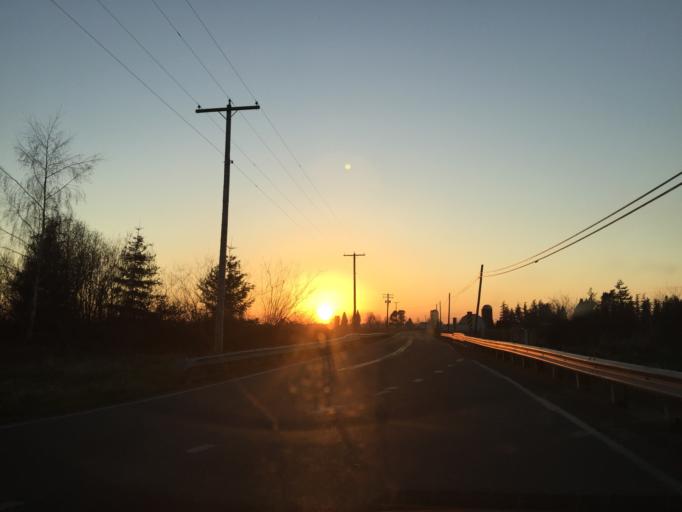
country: US
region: Washington
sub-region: Whatcom County
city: Sumas
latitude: 48.9818
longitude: -122.2379
